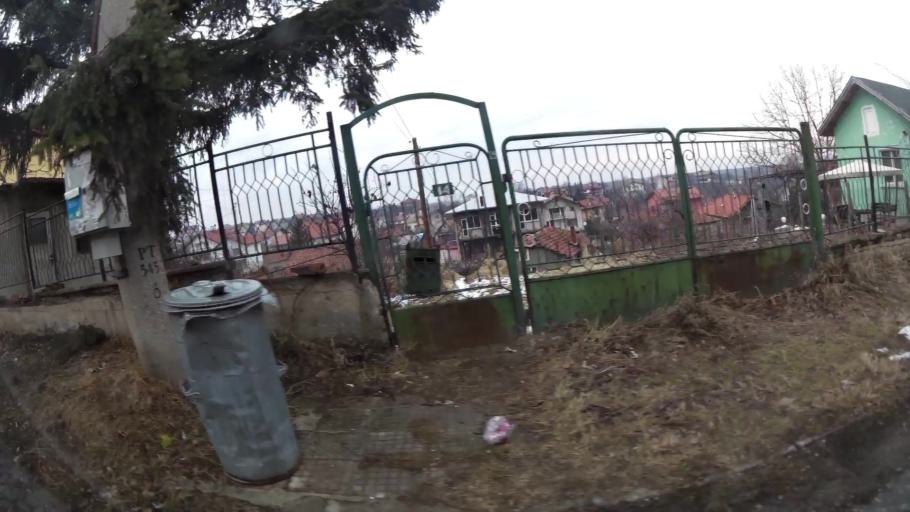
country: BG
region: Sofiya
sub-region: Obshtina Bozhurishte
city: Bozhurishte
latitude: 42.6974
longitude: 23.2263
